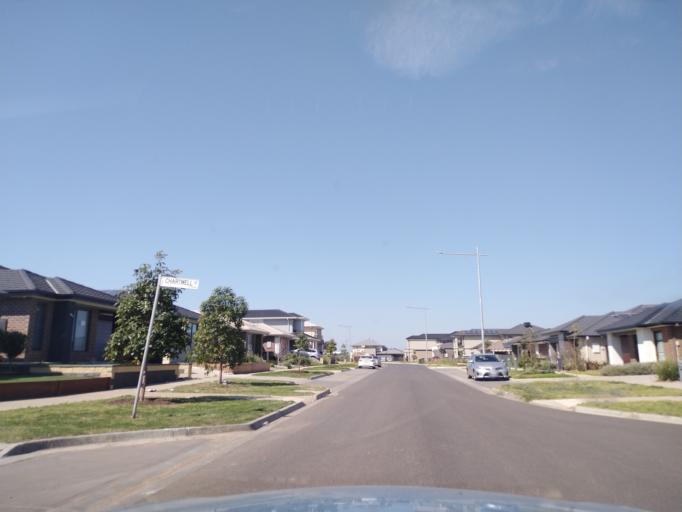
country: AU
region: Victoria
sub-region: Wyndham
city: Williams Landing
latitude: -37.8413
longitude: 144.7416
